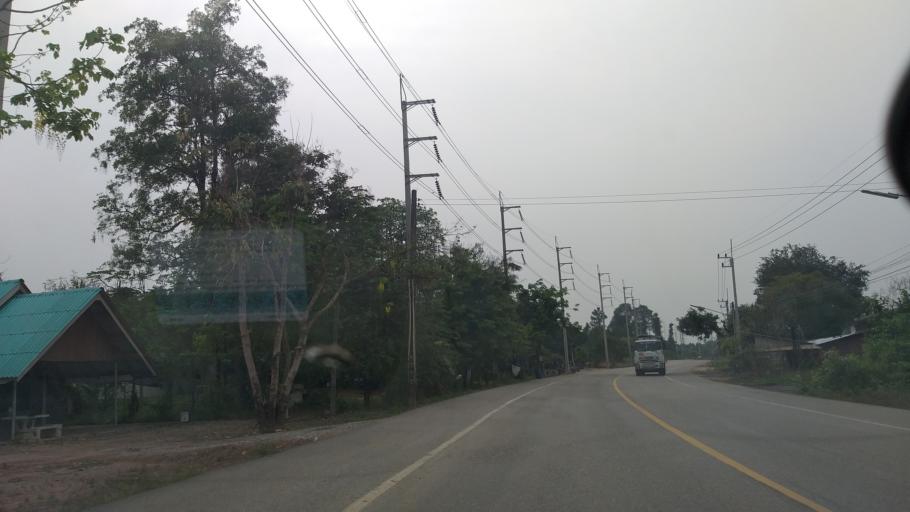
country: TH
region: Chachoengsao
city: Plaeng Yao
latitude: 13.5699
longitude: 101.2671
